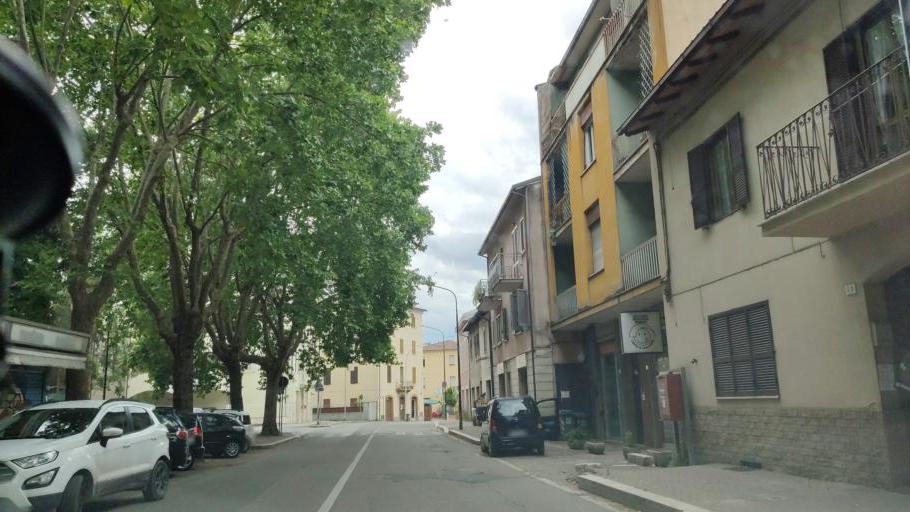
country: IT
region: Umbria
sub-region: Provincia di Terni
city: Terni
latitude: 42.5708
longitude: 12.6672
